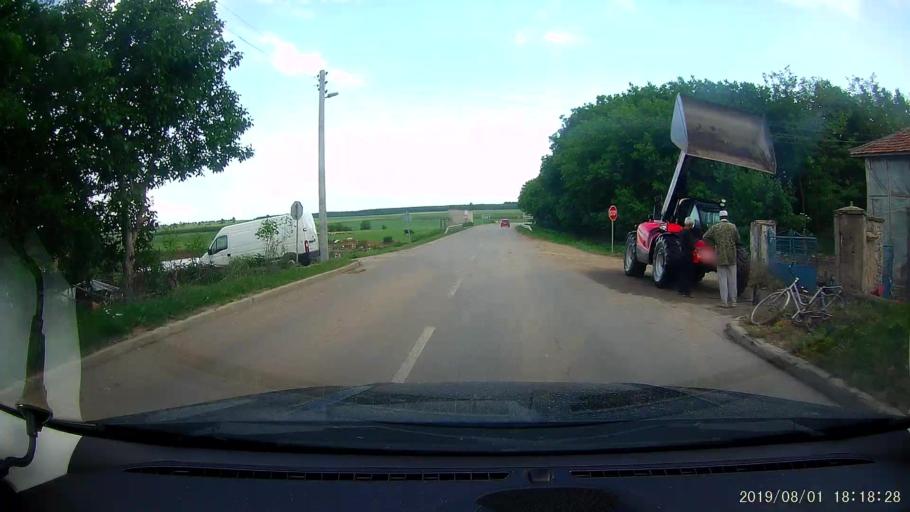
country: BG
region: Shumen
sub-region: Obshtina Kaolinovo
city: Kaolinovo
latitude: 43.6979
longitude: 27.0816
